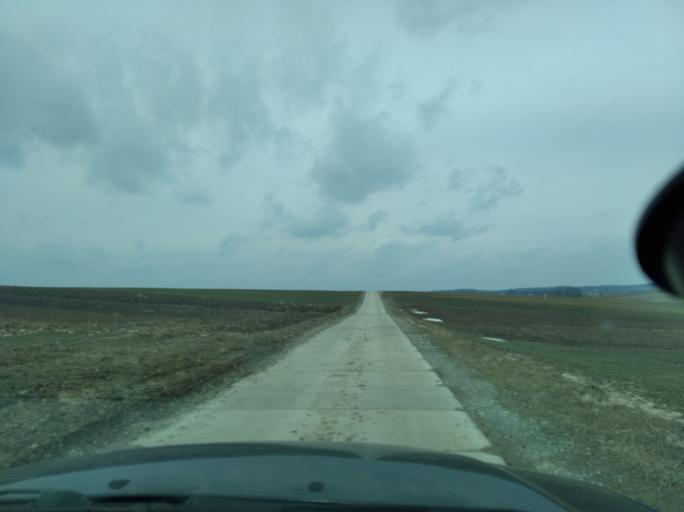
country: PL
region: Subcarpathian Voivodeship
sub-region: Powiat jaroslawski
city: Rokietnica
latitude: 49.9307
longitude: 22.5921
